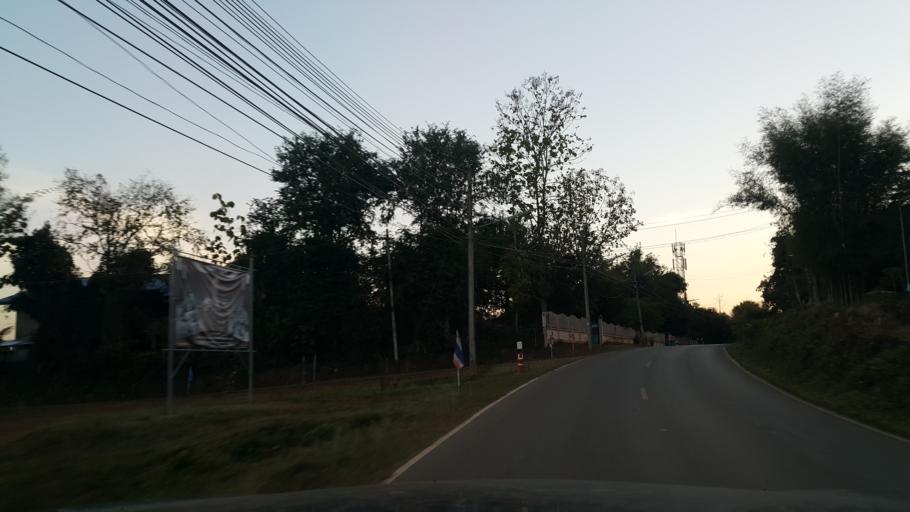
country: TH
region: Uttaradit
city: Uttaradit
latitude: 17.6577
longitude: 100.0932
